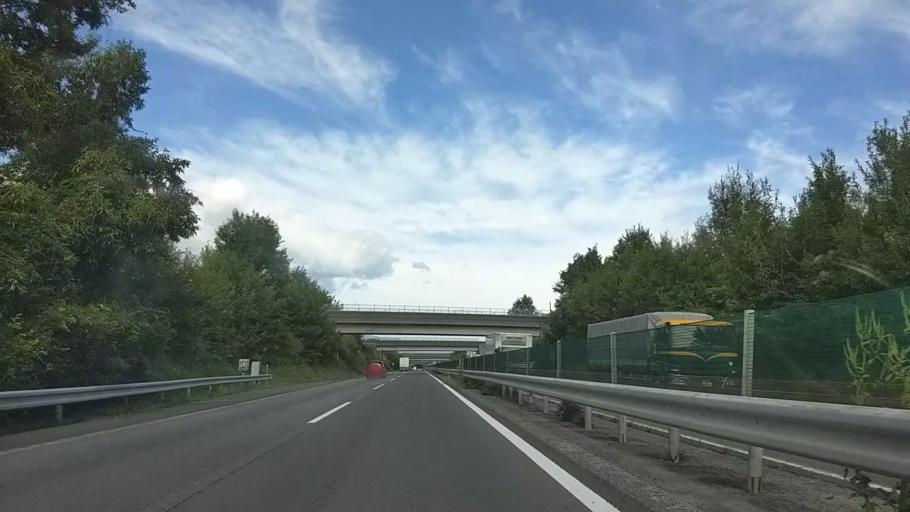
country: JP
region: Yamanashi
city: Nirasaki
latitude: 35.6976
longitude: 138.4859
